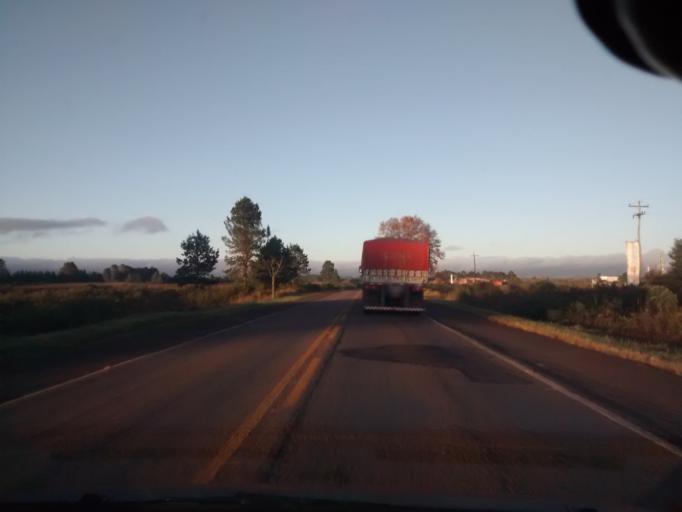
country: BR
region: Rio Grande do Sul
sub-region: Vacaria
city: Vacaria
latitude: -28.4036
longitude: -50.8549
